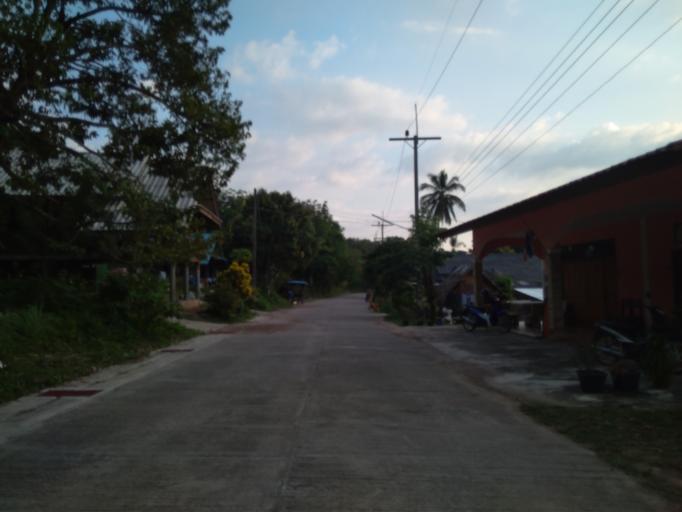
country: TH
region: Phangnga
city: Ko Yao
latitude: 8.1431
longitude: 98.5988
